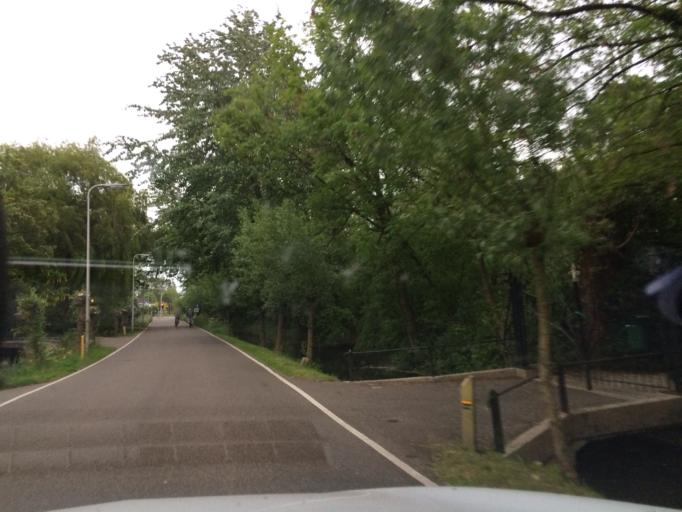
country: NL
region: South Holland
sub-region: Gemeente Capelle aan den IJssel
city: Capelle aan den IJssel
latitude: 51.9334
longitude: 4.5805
